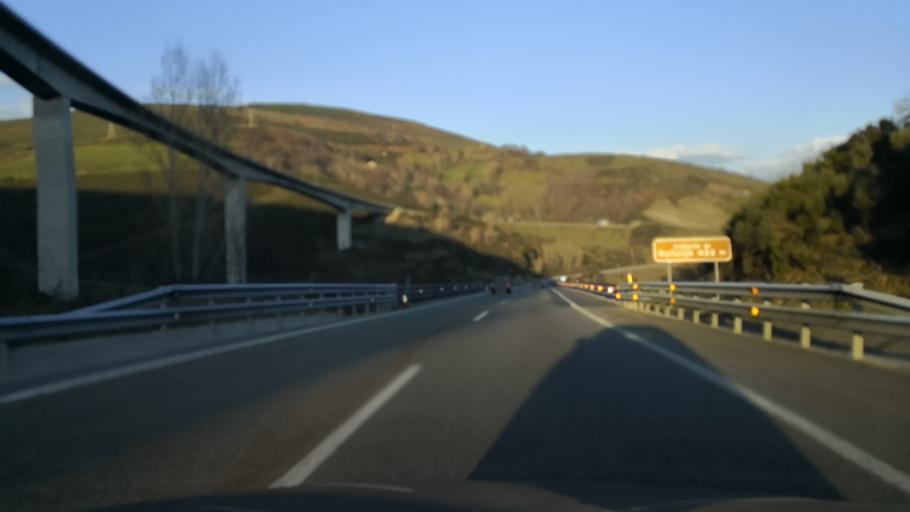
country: ES
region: Castille and Leon
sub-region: Provincia de Leon
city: Vega de Valcarce
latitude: 42.6746
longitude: -6.9715
